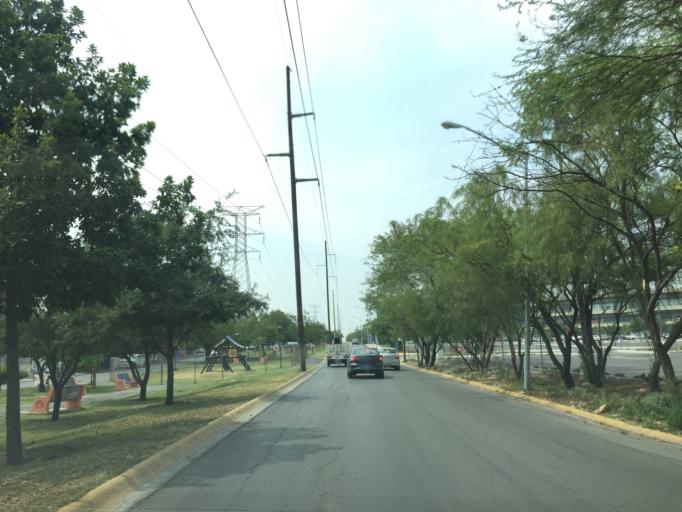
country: MX
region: Nuevo Leon
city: Guadalupe
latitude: 25.7169
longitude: -100.2200
